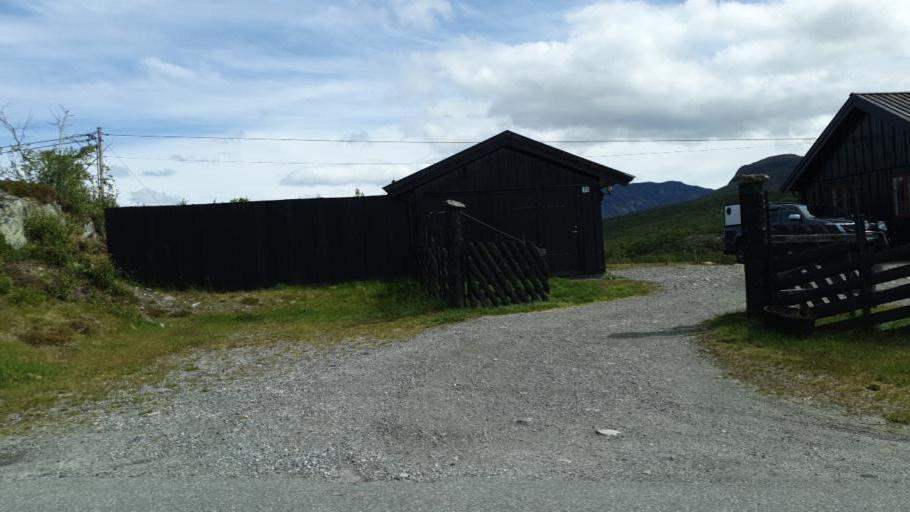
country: NO
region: Oppland
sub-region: Oystre Slidre
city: Heggenes
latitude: 61.4861
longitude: 8.8308
